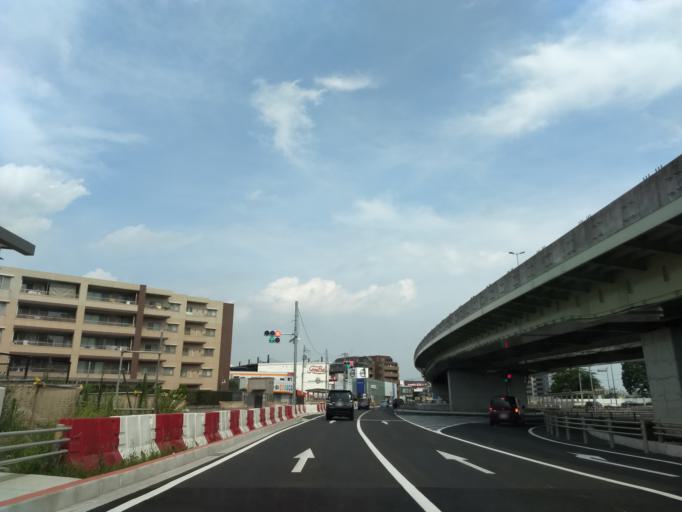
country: JP
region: Tokyo
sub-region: Machida-shi
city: Machida
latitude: 35.5131
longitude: 139.4701
